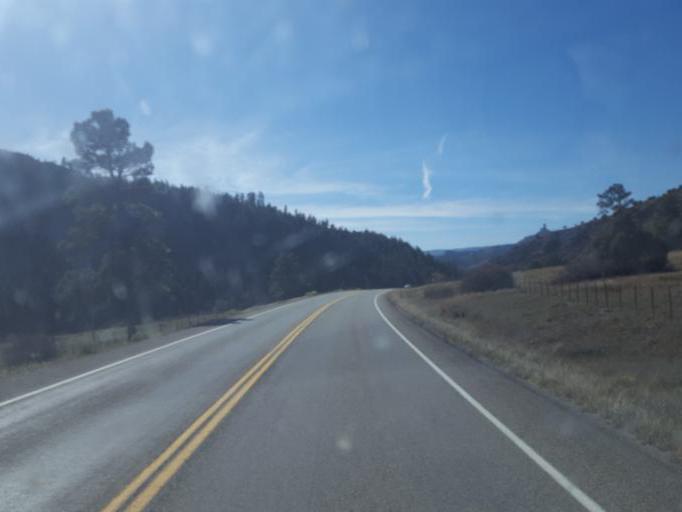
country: US
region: Colorado
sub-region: Archuleta County
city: Pagosa Springs
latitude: 37.2131
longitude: -107.2308
